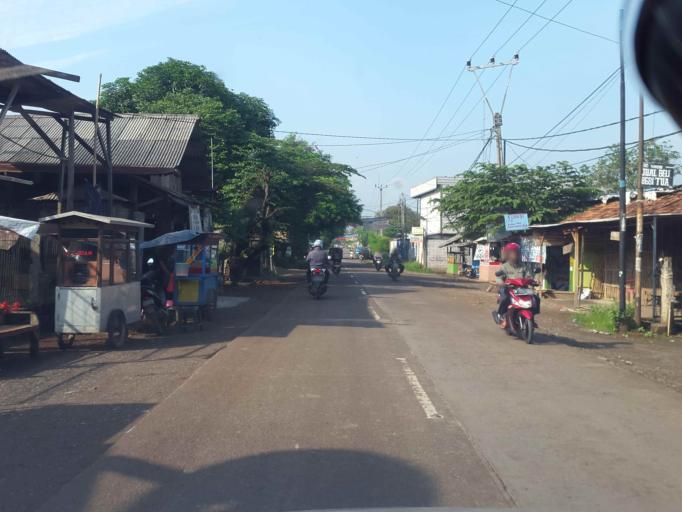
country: ID
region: West Java
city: Cileungsir
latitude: -6.3491
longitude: 107.0324
